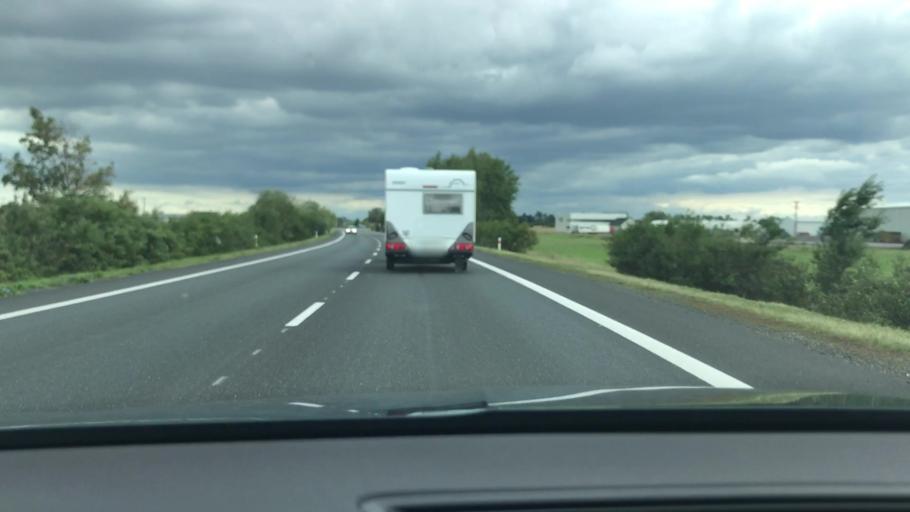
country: CZ
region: Central Bohemia
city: Libice nad Cidlinou
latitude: 50.1405
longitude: 15.1725
